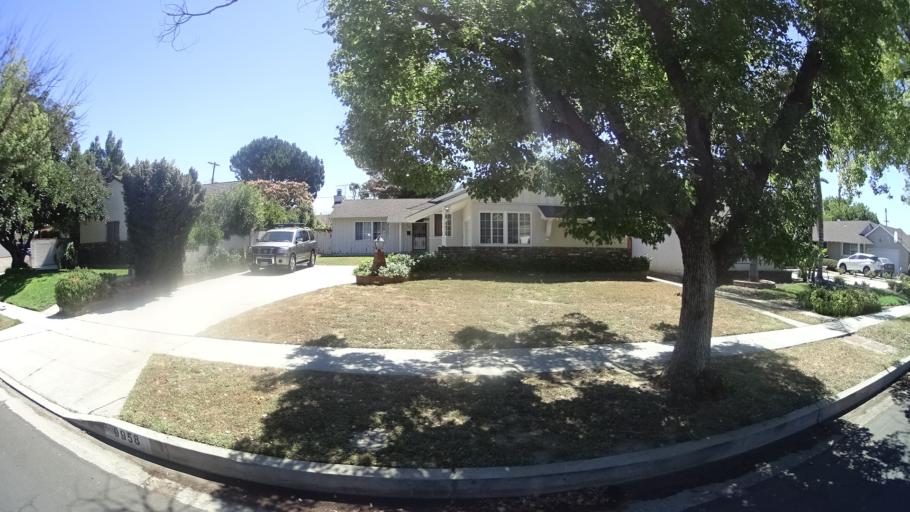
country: US
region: California
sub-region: Los Angeles County
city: San Fernando
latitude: 34.2517
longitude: -118.4652
